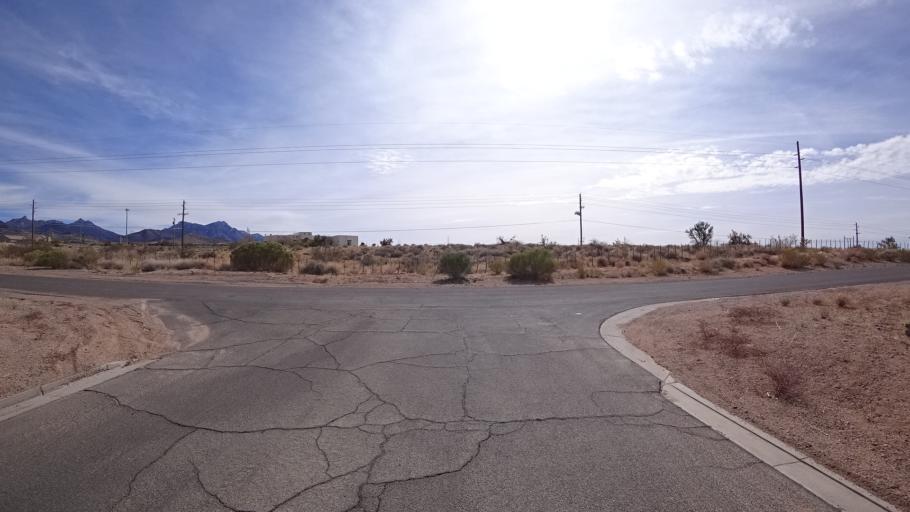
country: US
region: Arizona
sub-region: Mohave County
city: Kingman
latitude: 35.1815
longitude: -113.9861
